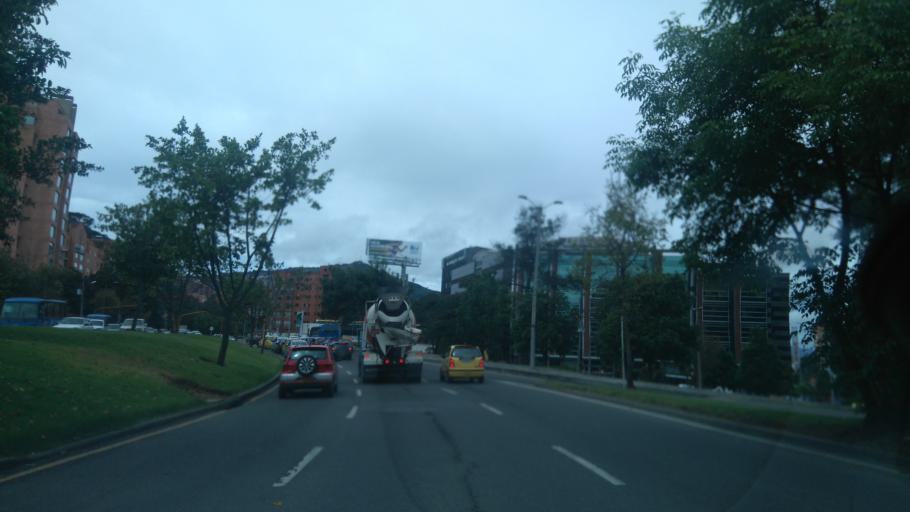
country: CO
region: Bogota D.C.
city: Barrio San Luis
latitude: 4.7129
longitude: -74.0294
